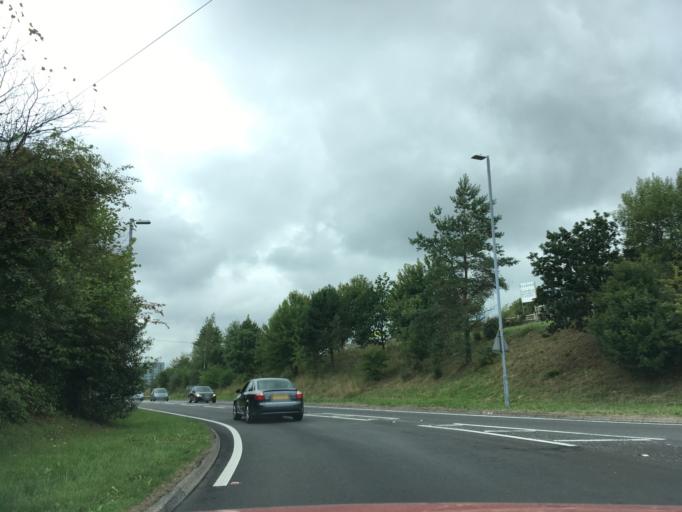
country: GB
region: Wales
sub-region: Carmarthenshire
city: Whitland
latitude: 51.8247
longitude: -4.5946
